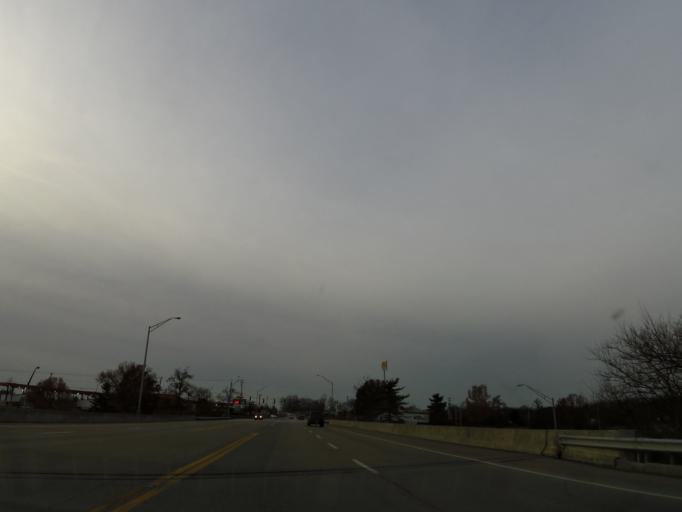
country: US
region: Kentucky
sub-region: Scott County
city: Georgetown
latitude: 38.2762
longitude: -84.5570
